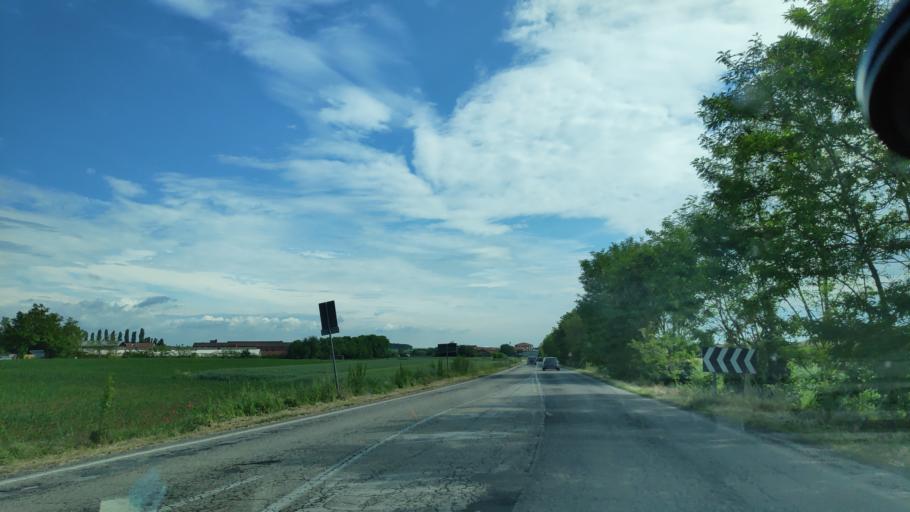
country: IT
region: Piedmont
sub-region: Provincia di Torino
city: Cambiano
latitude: 44.9810
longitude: 7.7846
